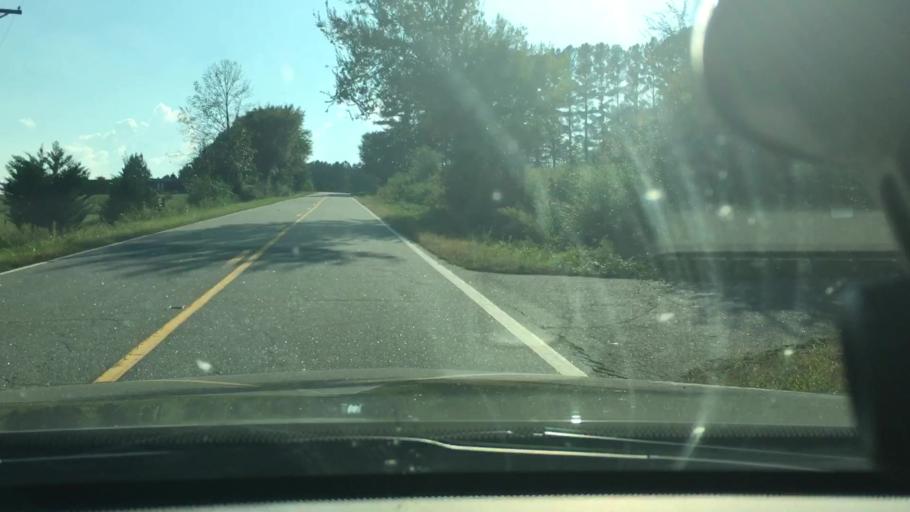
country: US
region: North Carolina
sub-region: Rutherford County
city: Rutherfordton
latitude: 35.3390
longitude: -82.0142
